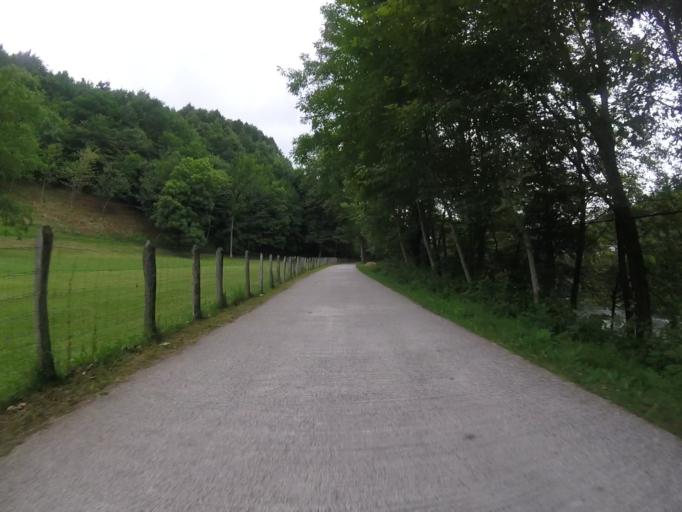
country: ES
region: Navarre
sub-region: Provincia de Navarra
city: Sunbilla
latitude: 43.1554
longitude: -1.6711
